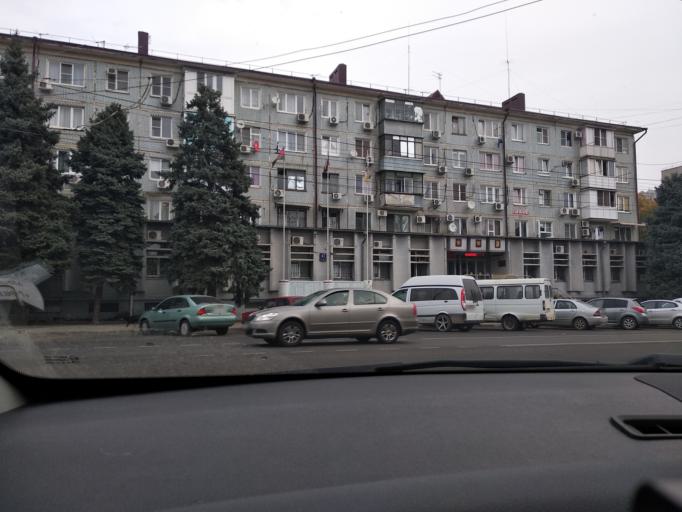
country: RU
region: Krasnodarskiy
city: Krasnodar
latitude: 45.0591
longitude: 38.9573
